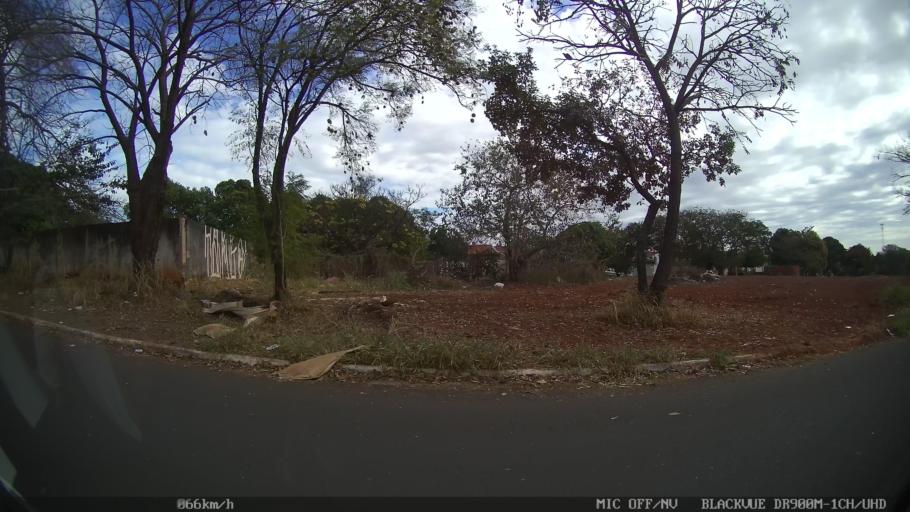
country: BR
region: Sao Paulo
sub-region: Sao Jose Do Rio Preto
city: Sao Jose do Rio Preto
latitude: -20.8068
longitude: -49.4914
